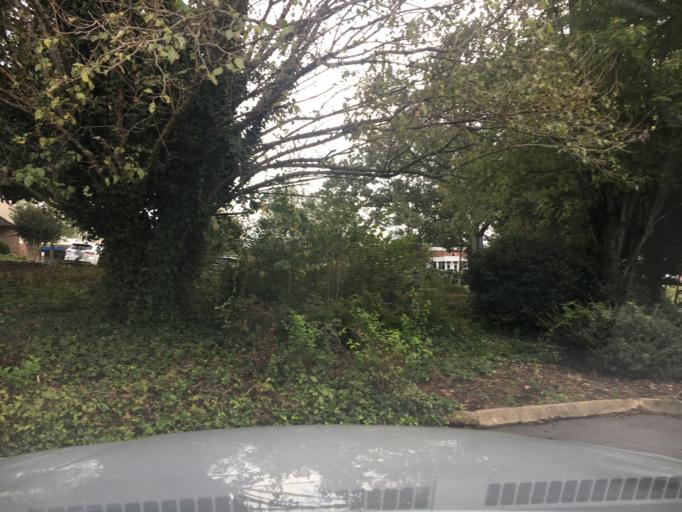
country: US
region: North Carolina
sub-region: Catawba County
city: Hickory
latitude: 35.7508
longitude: -81.3400
